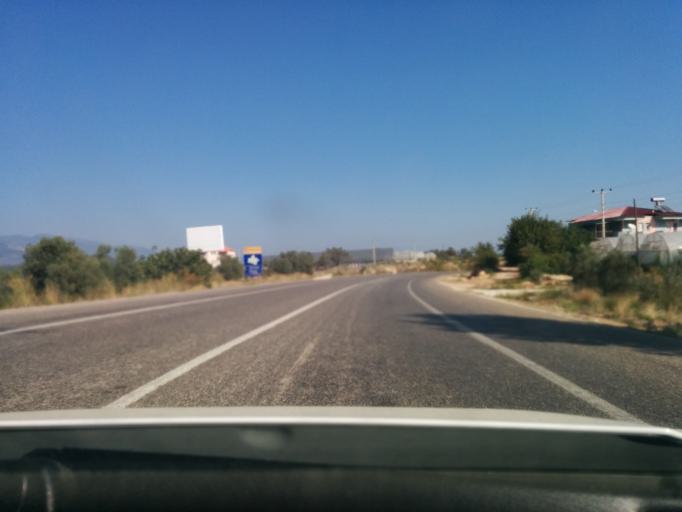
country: TR
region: Mugla
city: Esen
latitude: 36.3823
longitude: 29.3221
